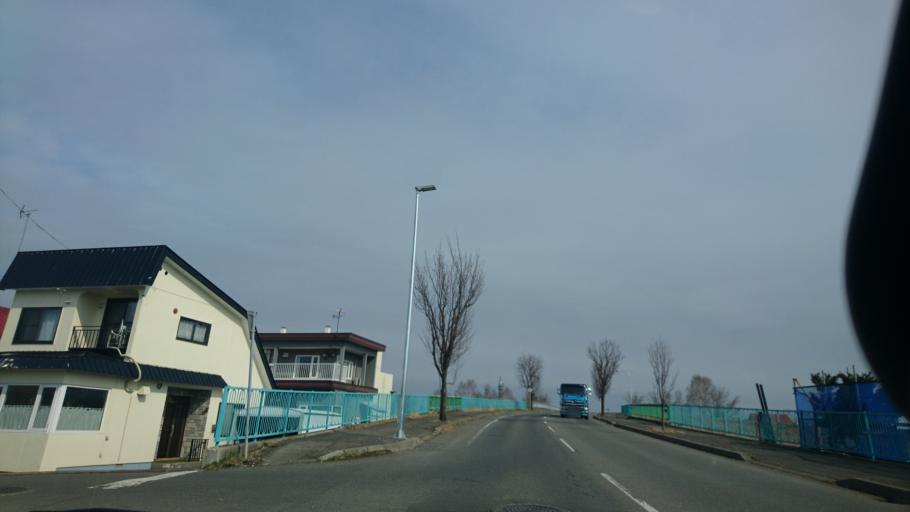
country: JP
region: Hokkaido
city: Obihiro
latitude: 42.9480
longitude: 143.2075
